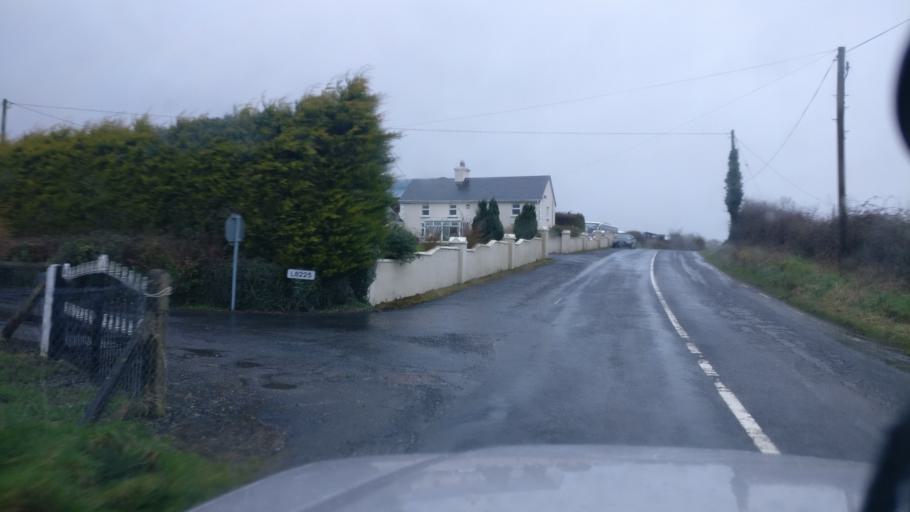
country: IE
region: Connaught
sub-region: County Galway
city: Loughrea
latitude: 53.0997
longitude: -8.4285
